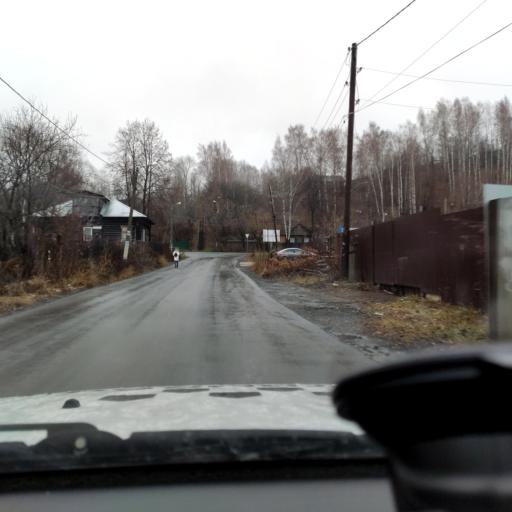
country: RU
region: Perm
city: Perm
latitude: 58.0570
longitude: 56.3339
